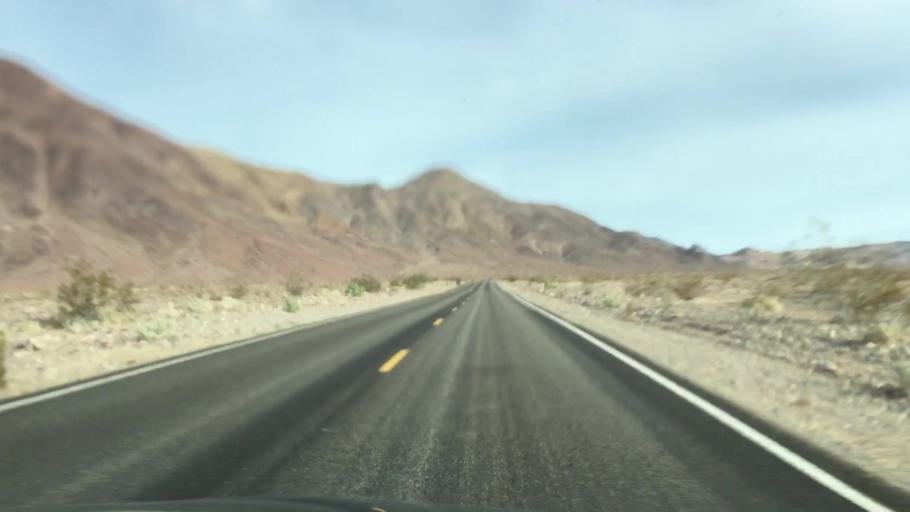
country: US
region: Nevada
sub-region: Nye County
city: Beatty
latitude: 36.6958
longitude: -117.0008
